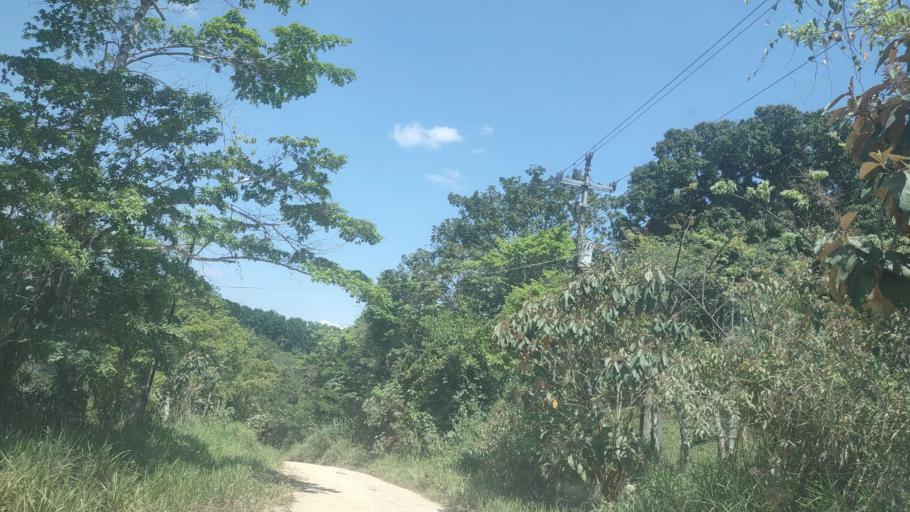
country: MX
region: Veracruz
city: Las Choapas
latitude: 17.7932
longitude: -94.1420
